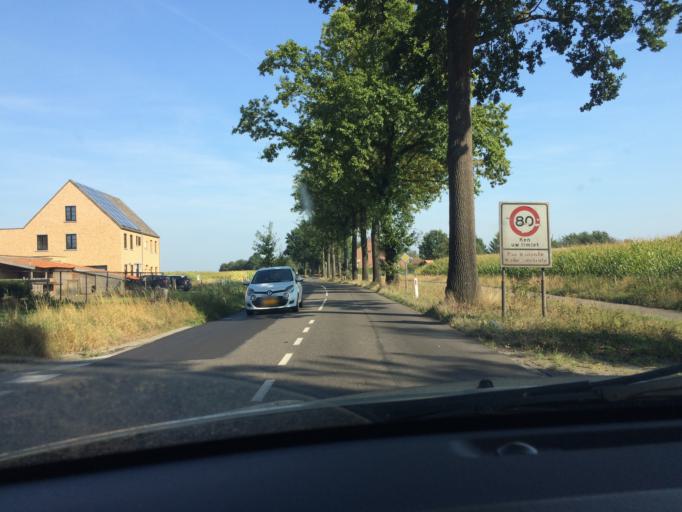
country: NL
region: North Brabant
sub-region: Gemeente Baarle-Nassau
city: Baarle-Nassau
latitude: 51.4476
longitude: 4.9369
